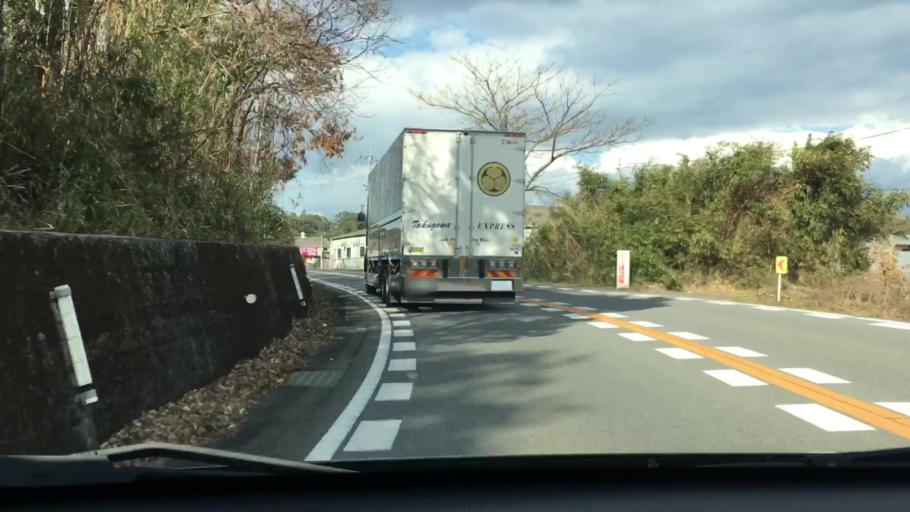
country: JP
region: Oita
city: Usuki
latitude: 33.0277
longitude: 131.6948
